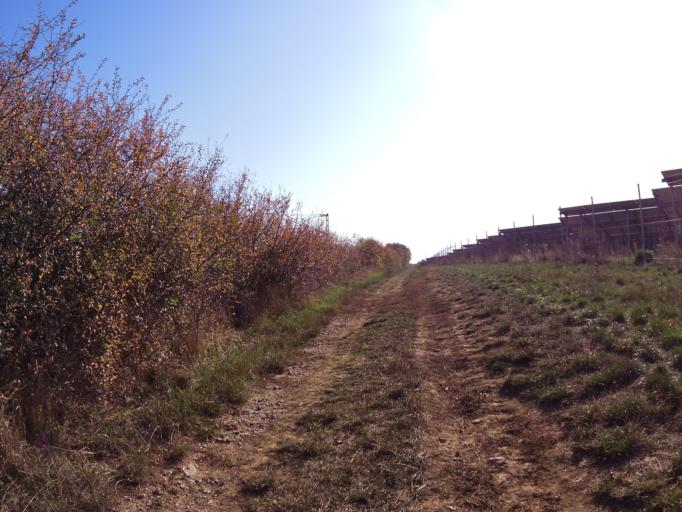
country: DE
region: Bavaria
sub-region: Regierungsbezirk Unterfranken
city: Reichenberg
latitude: 49.7169
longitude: 9.9186
